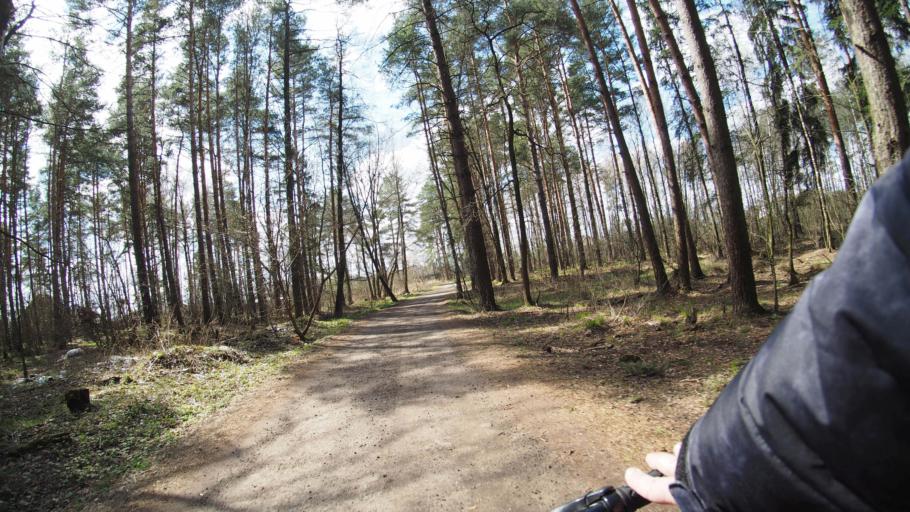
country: RU
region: Moskovskaya
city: Malyshevo
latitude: 55.5457
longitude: 38.3229
